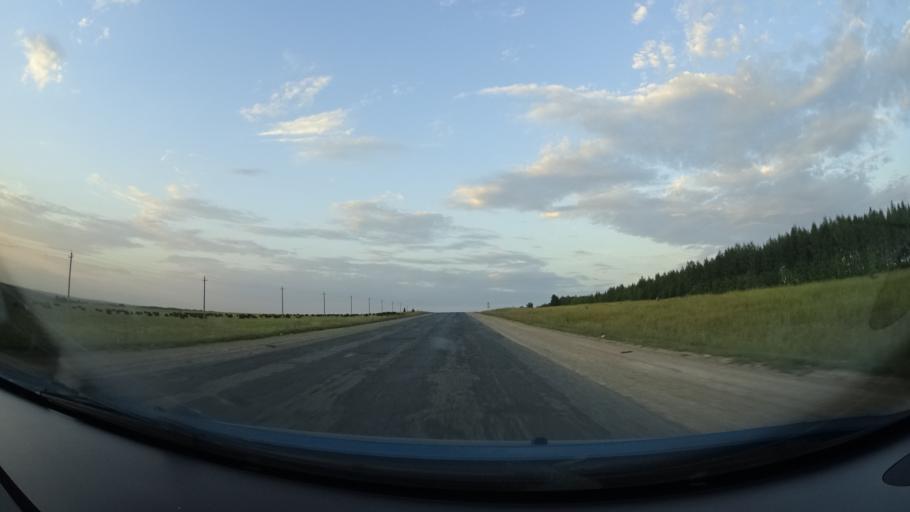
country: RU
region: Orenburg
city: Severnoye
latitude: 54.2340
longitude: 52.7769
